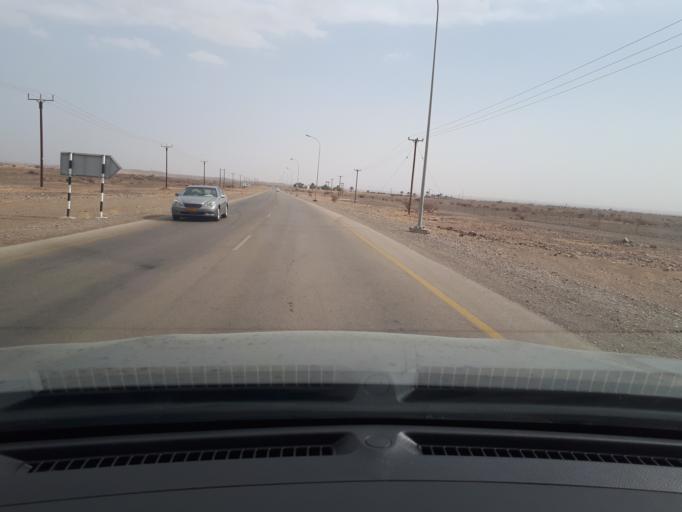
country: OM
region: Ash Sharqiyah
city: Badiyah
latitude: 22.5195
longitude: 58.9486
